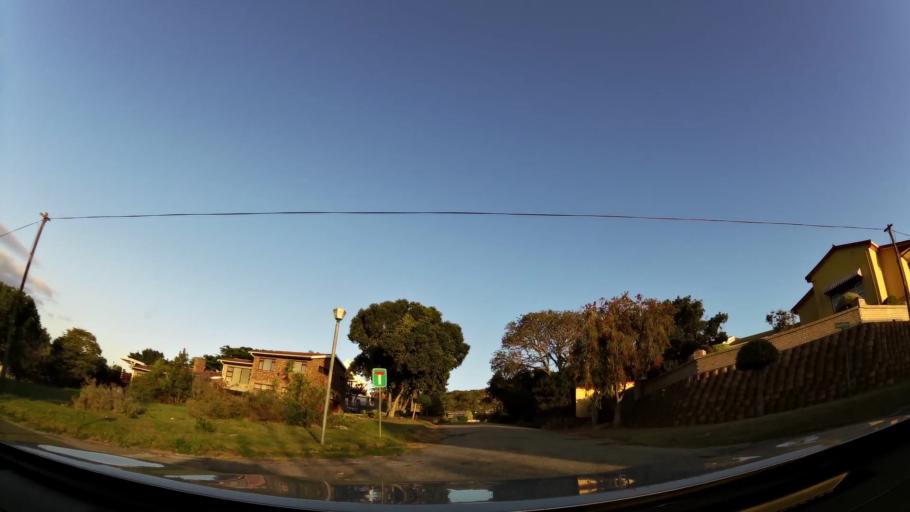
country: ZA
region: Western Cape
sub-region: Eden District Municipality
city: Knysna
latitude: -34.0216
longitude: 22.8132
